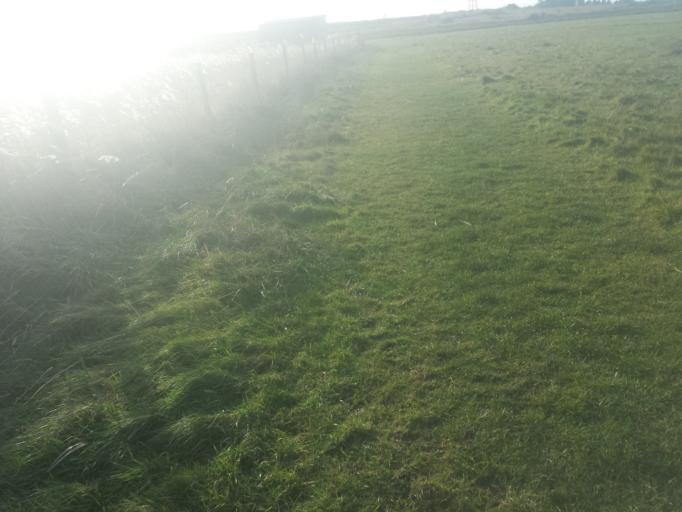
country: GB
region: England
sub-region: Essex
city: Frinton-on-Sea
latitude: 51.8135
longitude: 1.2236
